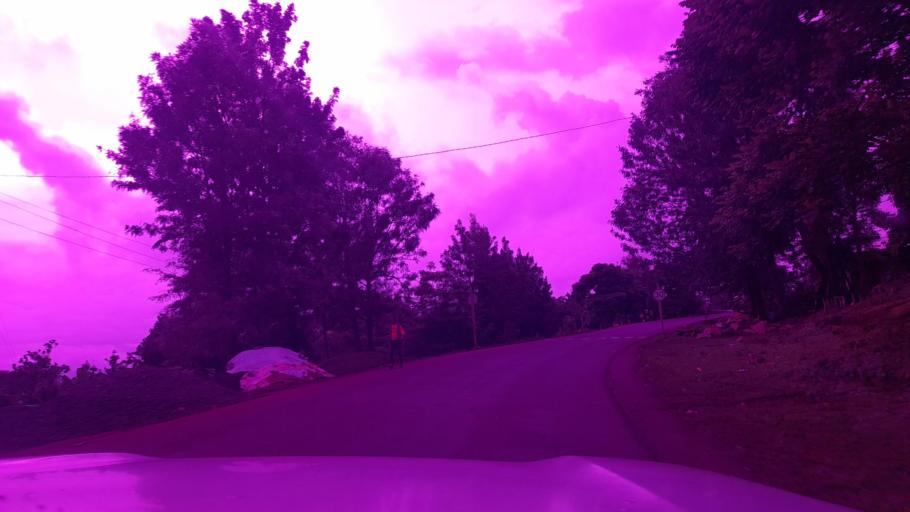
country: ET
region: Oromiya
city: Jima
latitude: 7.9614
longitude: 37.4415
